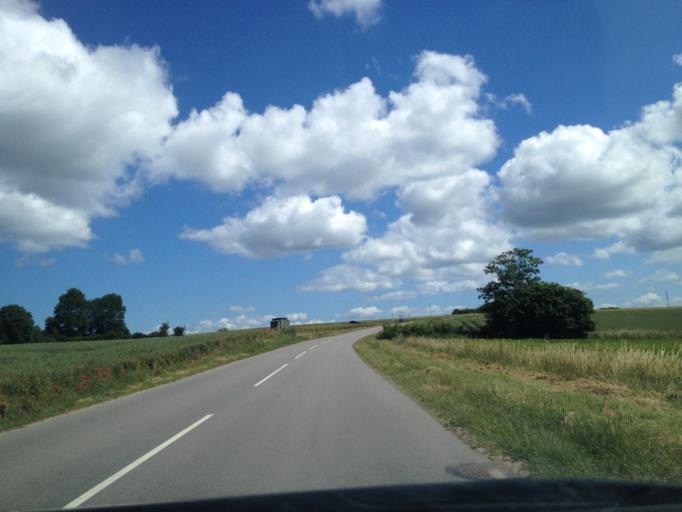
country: DK
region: Zealand
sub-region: Odsherred Kommune
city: Hojby
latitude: 55.9131
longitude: 11.5709
